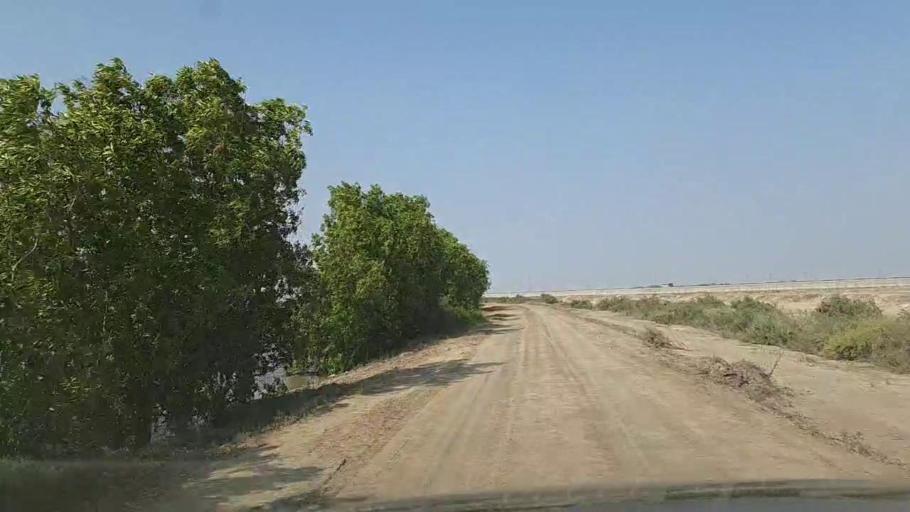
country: PK
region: Sindh
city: Gharo
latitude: 24.7068
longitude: 67.5566
